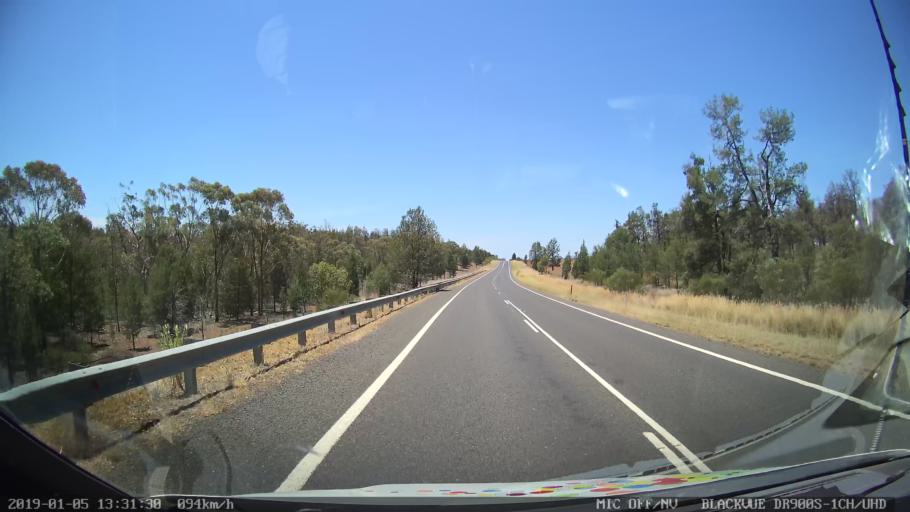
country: AU
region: New South Wales
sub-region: Gunnedah
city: Gunnedah
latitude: -31.0105
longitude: 150.0848
